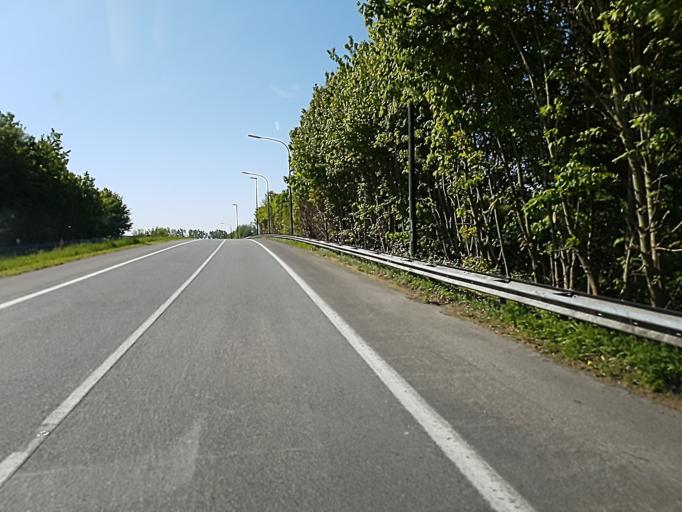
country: BE
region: Wallonia
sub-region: Province du Hainaut
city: Ath
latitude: 50.6676
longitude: 3.7971
